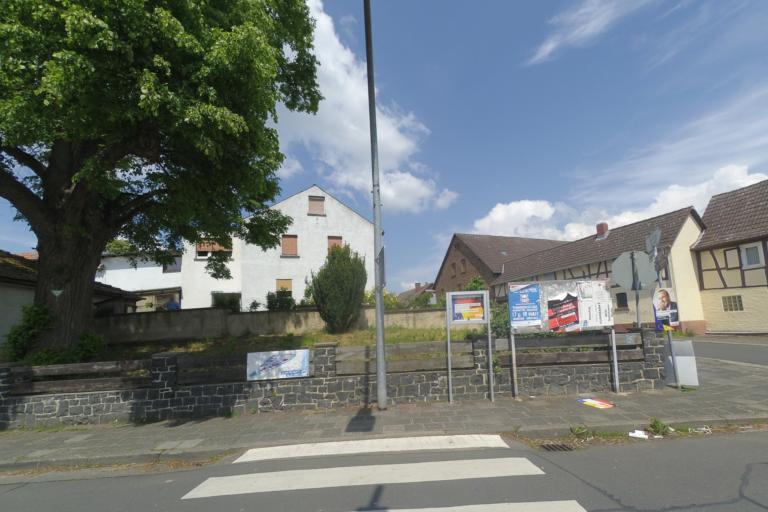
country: DE
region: Hesse
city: Nidderau
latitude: 50.2586
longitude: 8.9062
